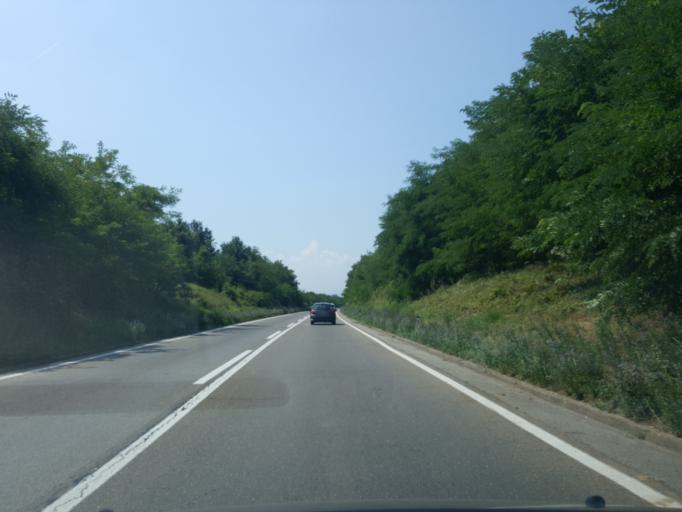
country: RS
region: Central Serbia
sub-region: Belgrade
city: Sopot
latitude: 44.5270
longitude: 20.6555
